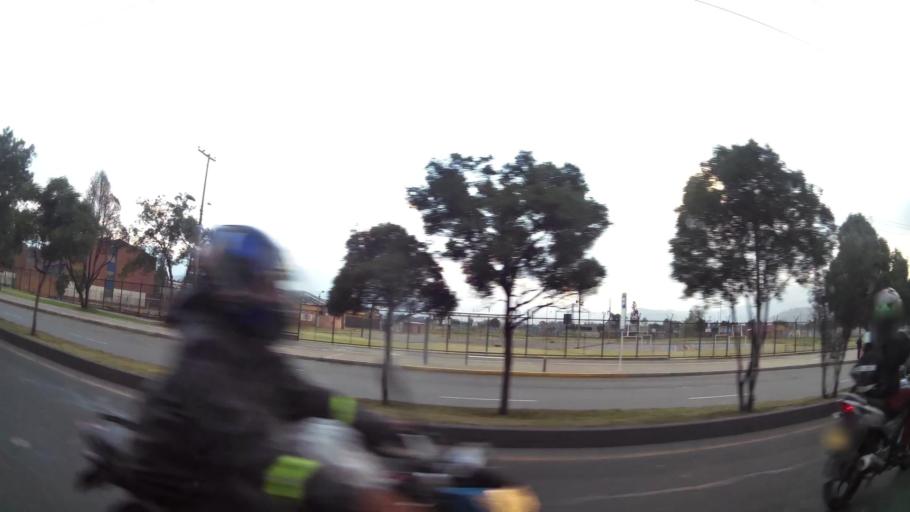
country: CO
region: Bogota D.C.
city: Bogota
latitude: 4.5756
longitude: -74.1336
